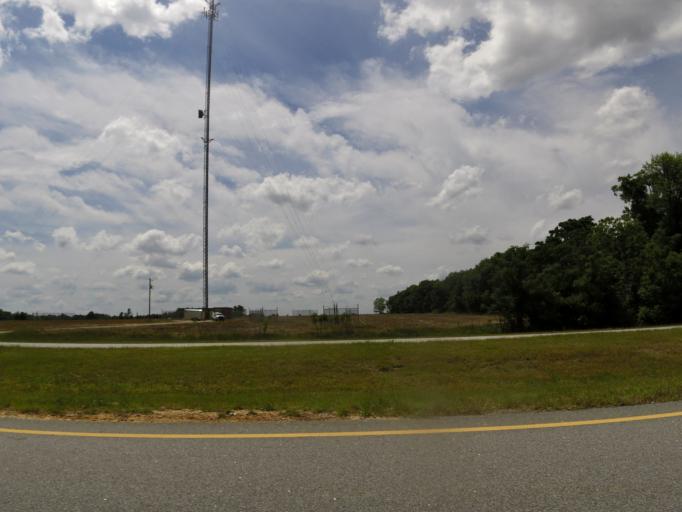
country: US
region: Georgia
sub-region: Emanuel County
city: Swainsboro
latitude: 32.6861
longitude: -82.3900
